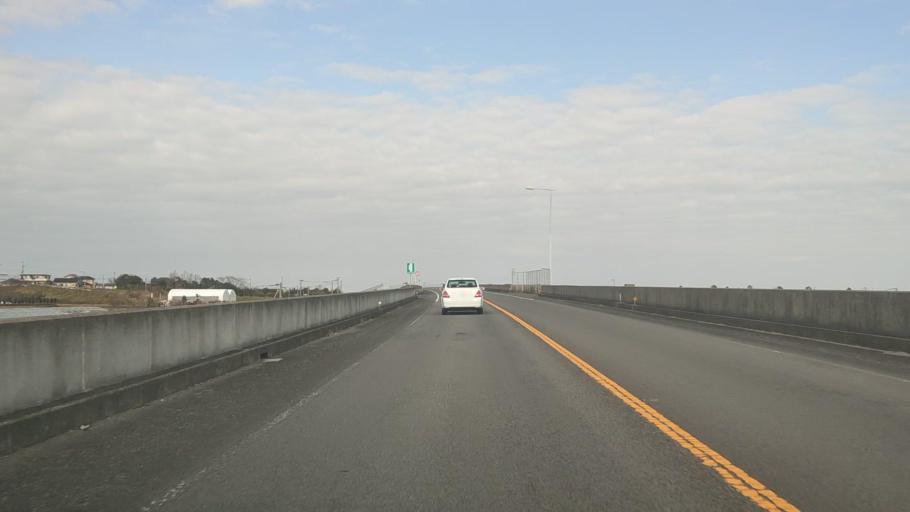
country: JP
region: Nagasaki
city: Shimabara
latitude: 32.7367
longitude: 130.3702
